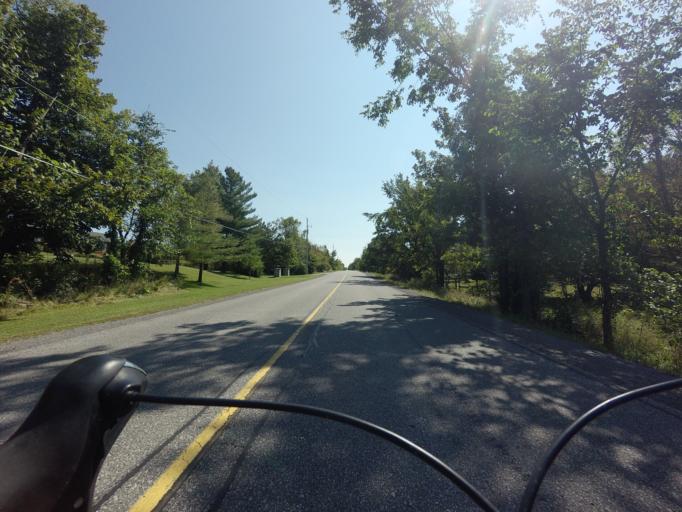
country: CA
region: Ontario
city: Bells Corners
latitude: 45.3998
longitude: -76.0186
